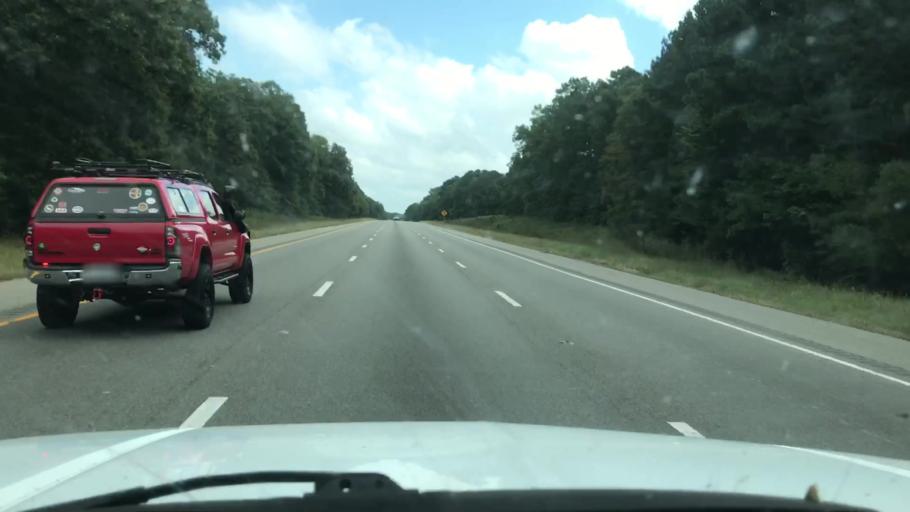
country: US
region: Virginia
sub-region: Henrico County
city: Short Pump
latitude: 37.6712
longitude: -77.5782
